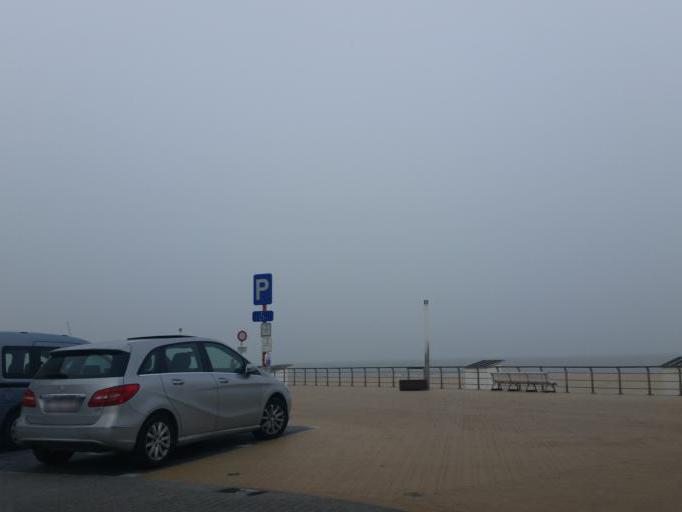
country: BE
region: Flanders
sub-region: Provincie West-Vlaanderen
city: Ostend
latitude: 51.2182
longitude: 2.8836
